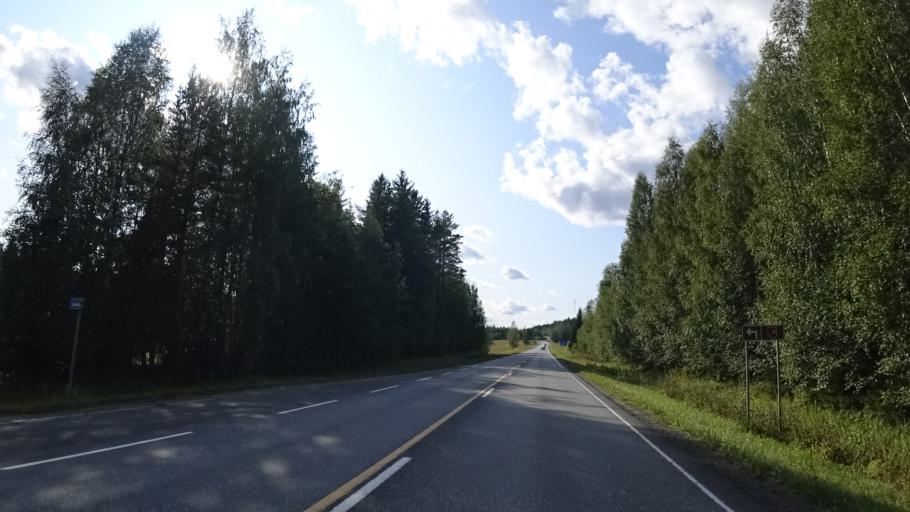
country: FI
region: North Karelia
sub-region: Keski-Karjala
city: Kitee
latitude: 62.0903
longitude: 29.9707
